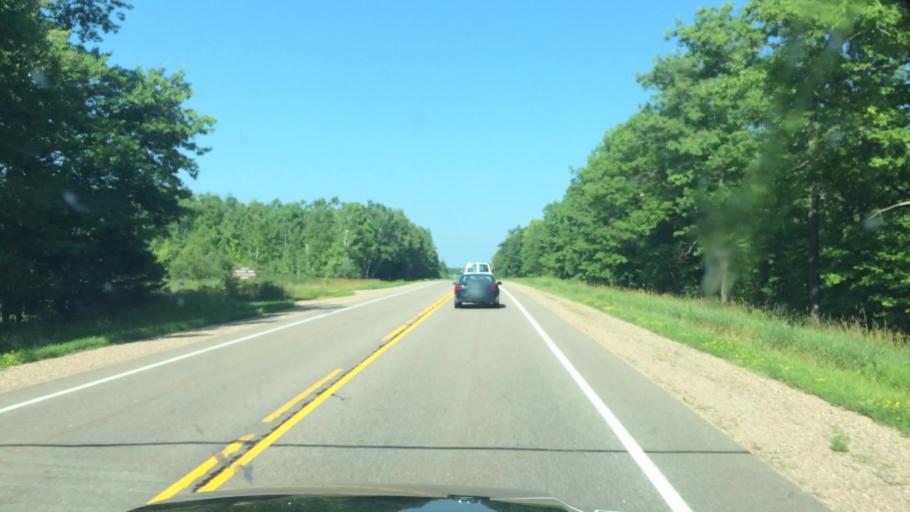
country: US
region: Wisconsin
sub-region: Langlade County
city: Antigo
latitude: 45.1470
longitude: -89.3849
